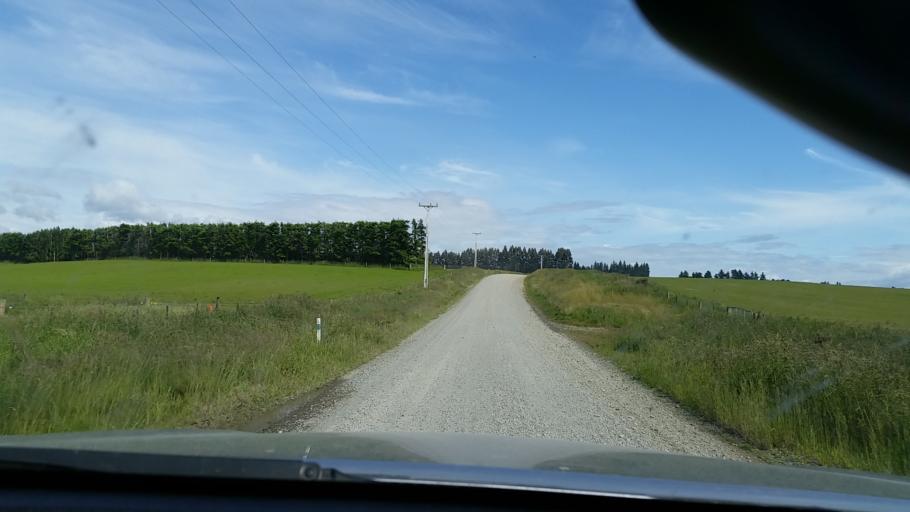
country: NZ
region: Southland
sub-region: Southland District
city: Winton
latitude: -45.6472
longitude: 168.2162
